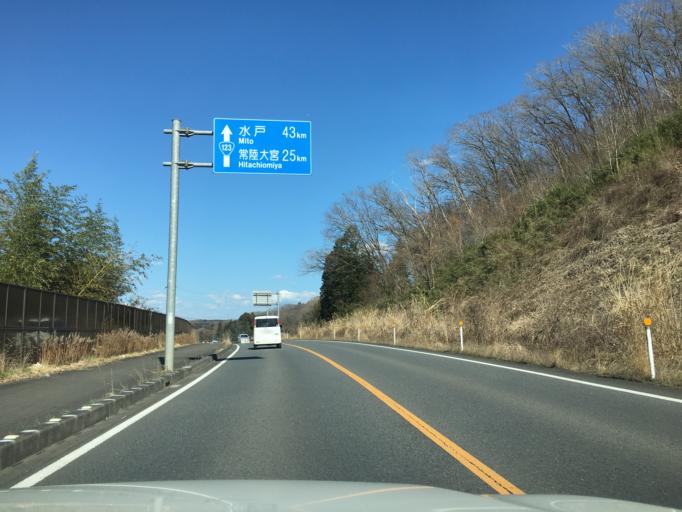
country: JP
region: Tochigi
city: Motegi
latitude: 36.5279
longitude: 140.1983
